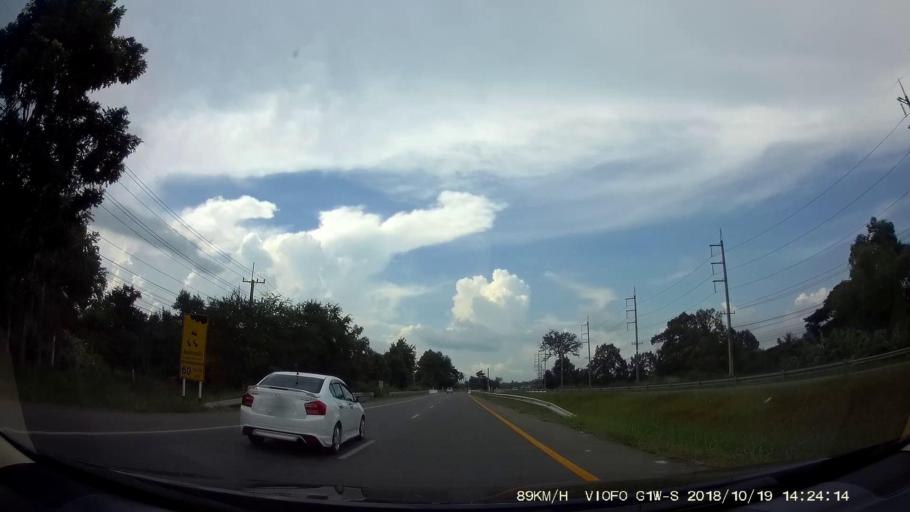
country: TH
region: Chaiyaphum
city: Kaeng Khro
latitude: 16.0786
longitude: 102.2748
